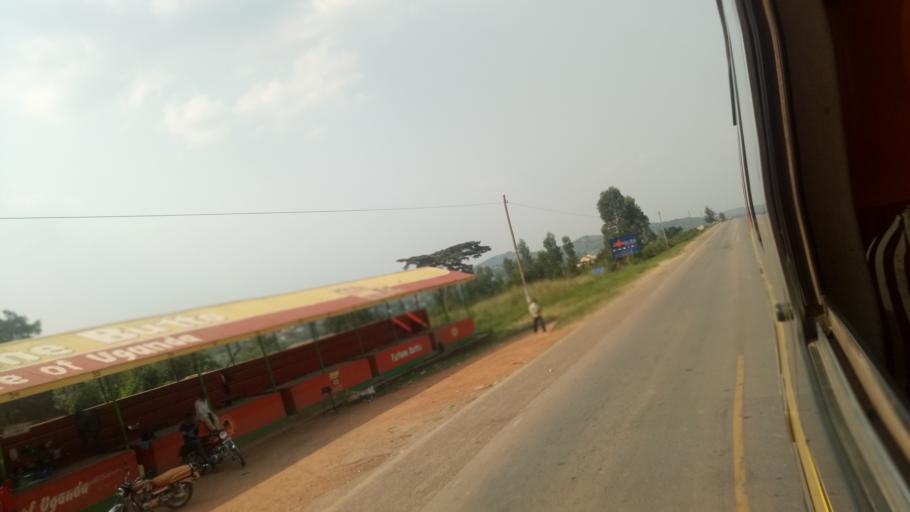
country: UG
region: Western Region
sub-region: Mbarara District
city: Mbarara
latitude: -0.5303
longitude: 30.7204
